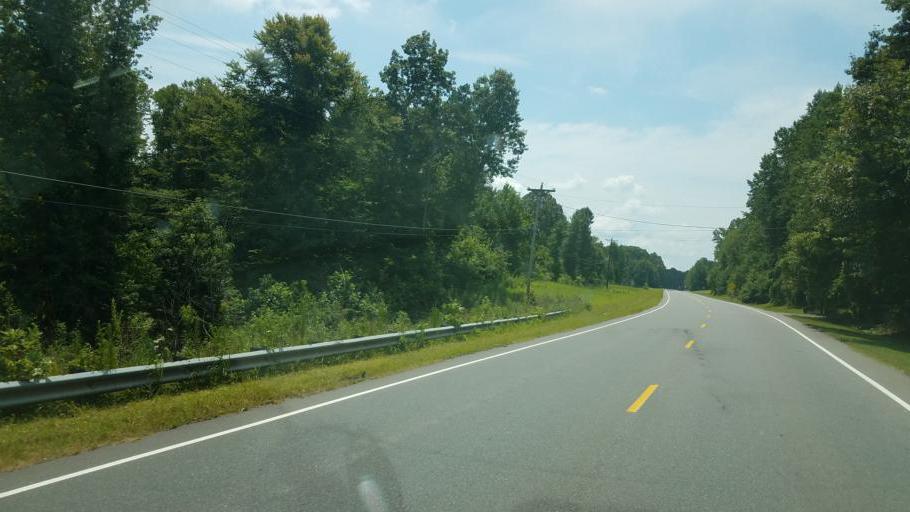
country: US
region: North Carolina
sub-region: Cleveland County
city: Kings Mountain
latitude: 35.2017
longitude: -81.3412
